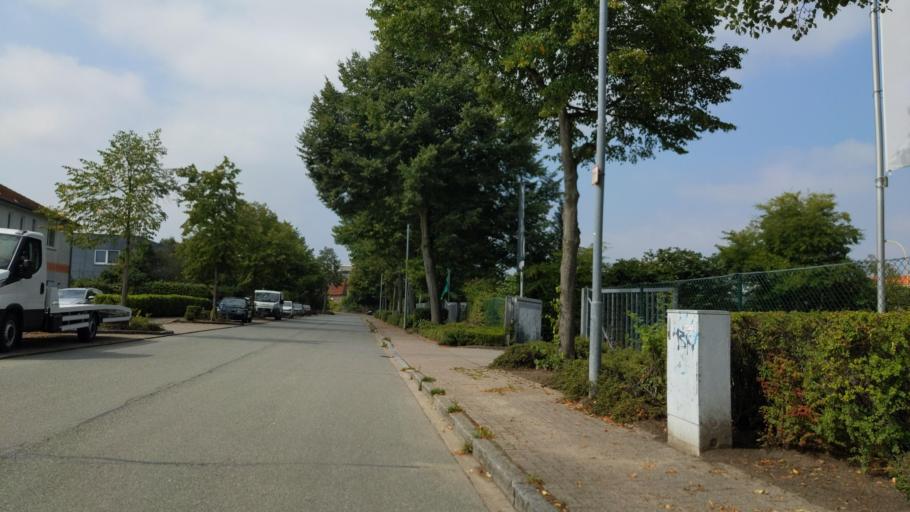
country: DE
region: Schleswig-Holstein
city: Stockelsdorf
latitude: 53.8930
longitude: 10.6231
